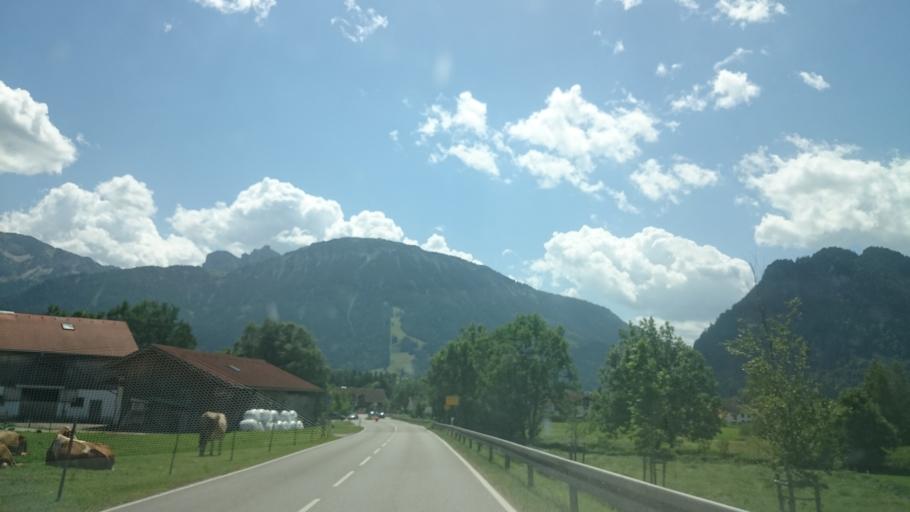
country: DE
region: Bavaria
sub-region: Swabia
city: Pfronten
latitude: 47.5861
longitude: 10.5674
